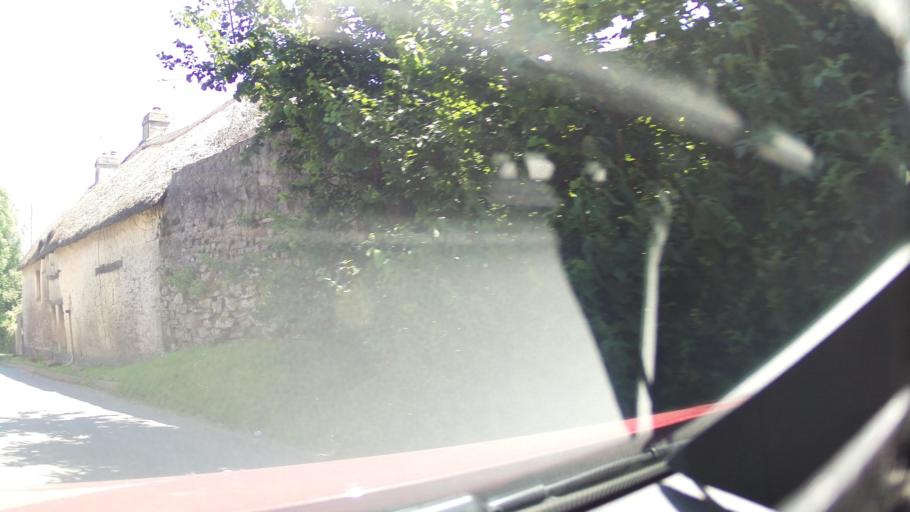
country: GB
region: England
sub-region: Devon
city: Ipplepen
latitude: 50.4828
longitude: -3.6114
